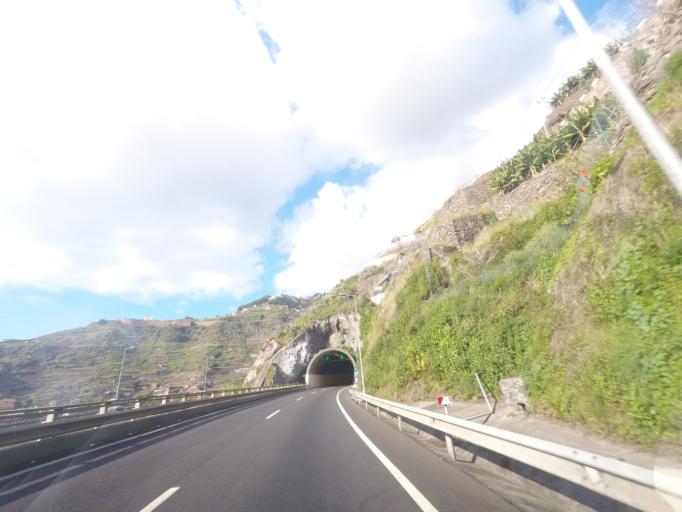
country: PT
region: Madeira
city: Camara de Lobos
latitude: 32.6593
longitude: -16.9911
